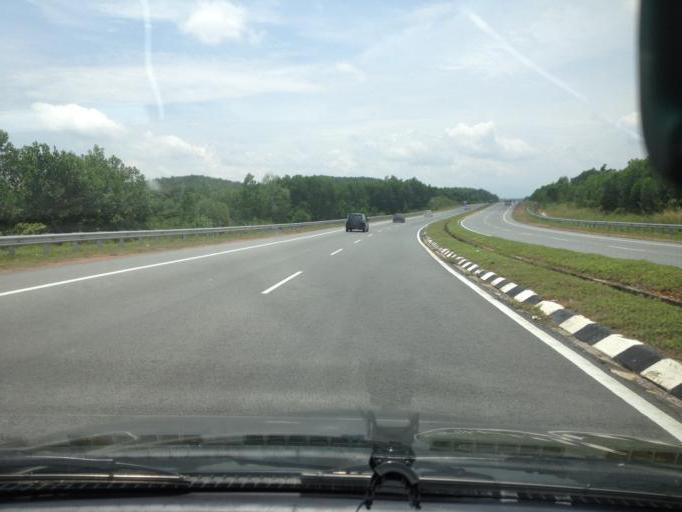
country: MY
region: Kedah
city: Sungai Petani
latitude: 5.6179
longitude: 100.5549
